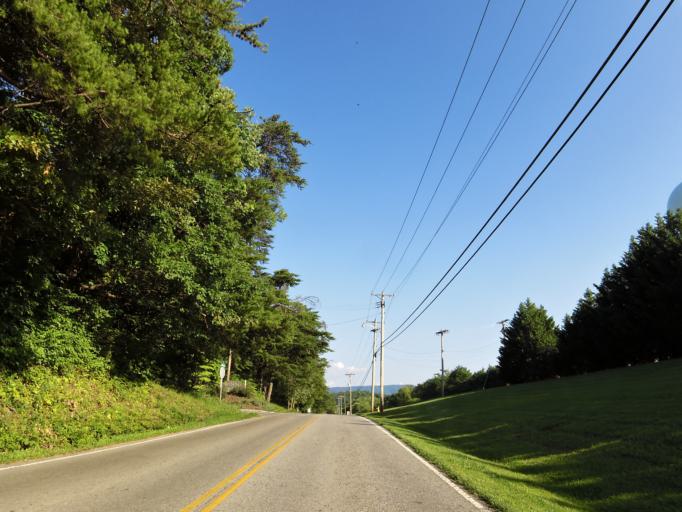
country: US
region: Tennessee
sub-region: Blount County
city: Maryville
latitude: 35.7339
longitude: -83.9511
